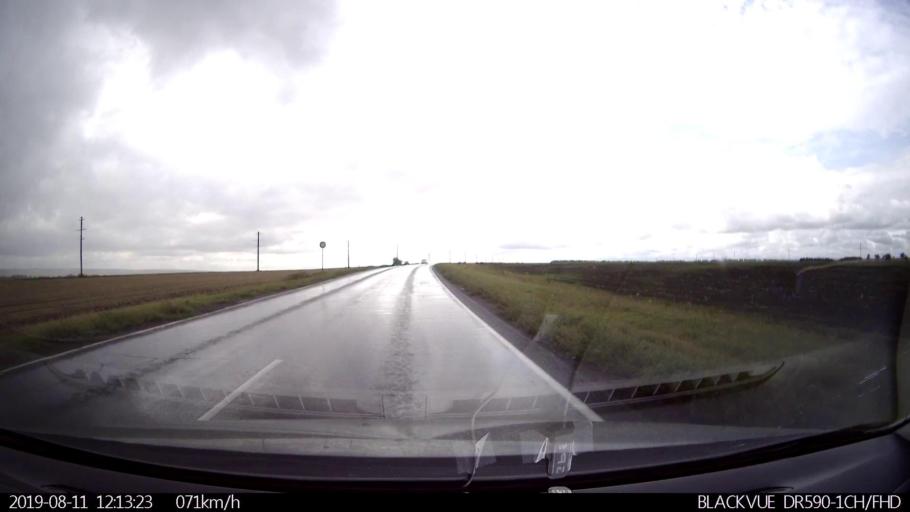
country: RU
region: Ulyanovsk
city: Silikatnyy
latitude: 53.9625
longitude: 47.9925
